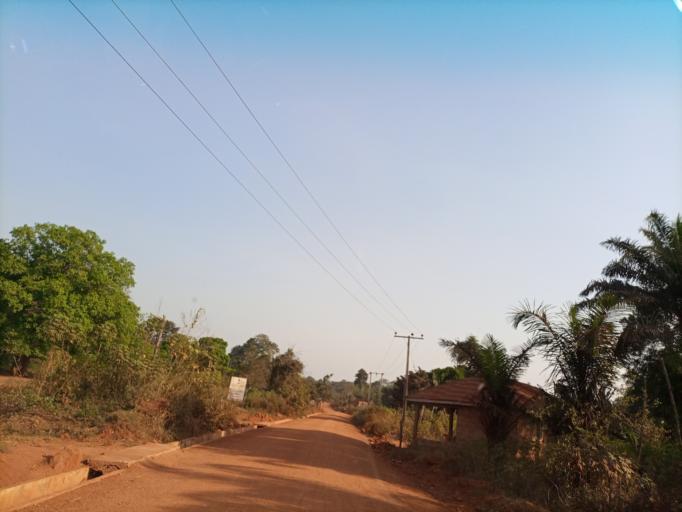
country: NG
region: Enugu
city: Opi
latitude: 6.7589
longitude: 7.4018
